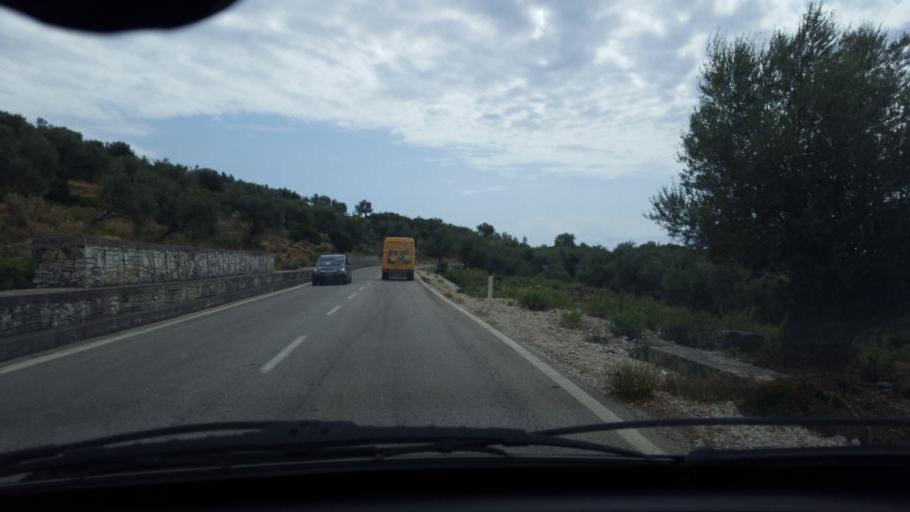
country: AL
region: Vlore
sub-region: Rrethi i Sarandes
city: Lukove
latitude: 40.0303
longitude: 19.8877
